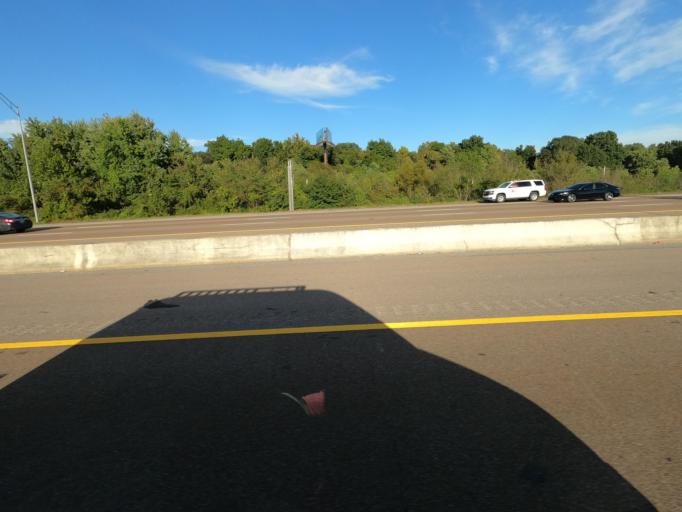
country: US
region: Tennessee
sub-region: Shelby County
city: Bartlett
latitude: 35.1864
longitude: -89.9156
